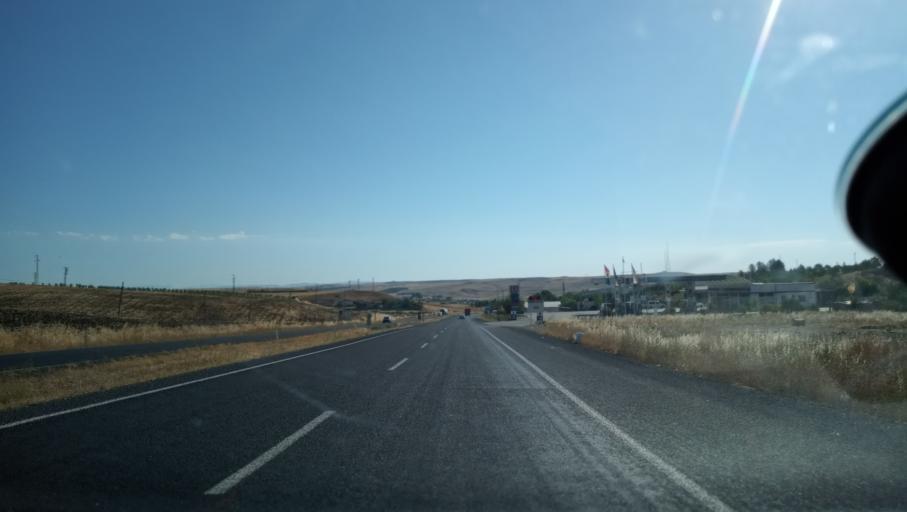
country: TR
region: Diyarbakir
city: Sur
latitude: 37.9875
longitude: 40.3707
